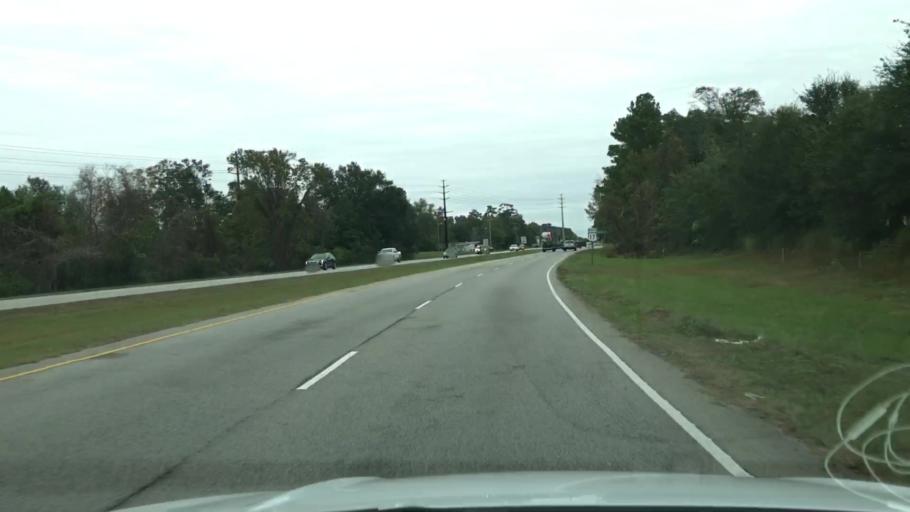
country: US
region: South Carolina
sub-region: Georgetown County
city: Murrells Inlet
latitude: 33.5299
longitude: -79.0616
